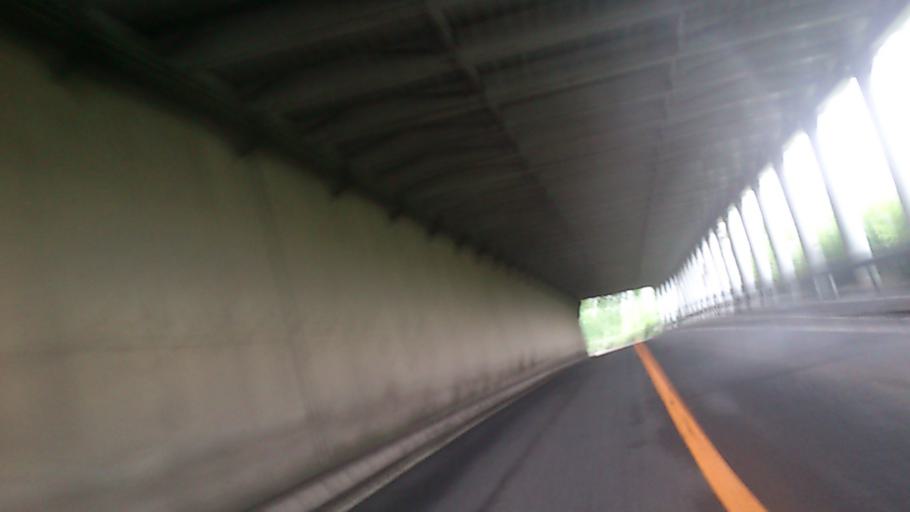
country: JP
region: Hokkaido
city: Niseko Town
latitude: 42.8047
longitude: 140.8907
